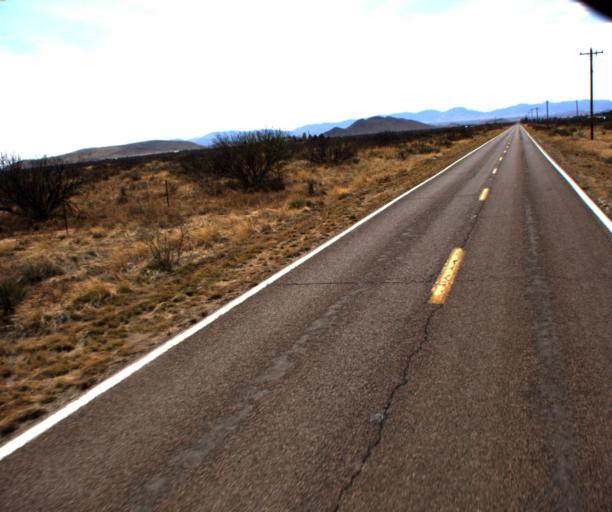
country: US
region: Arizona
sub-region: Cochise County
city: Willcox
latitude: 31.8762
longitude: -109.6032
